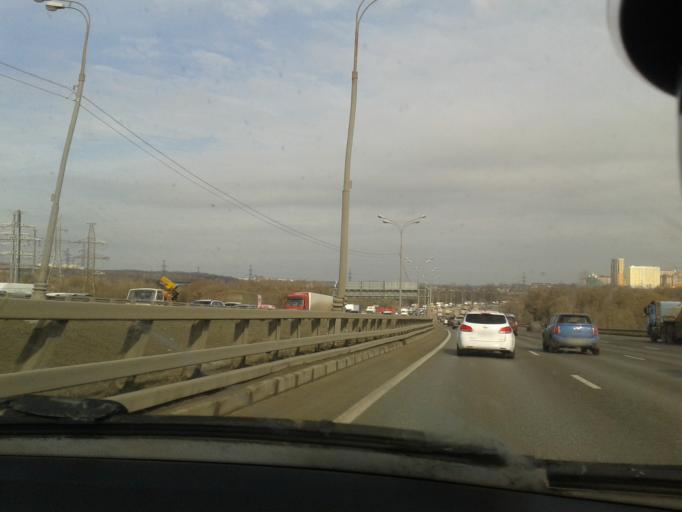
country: RU
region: Moscow
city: Strogino
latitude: 55.8407
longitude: 37.3951
